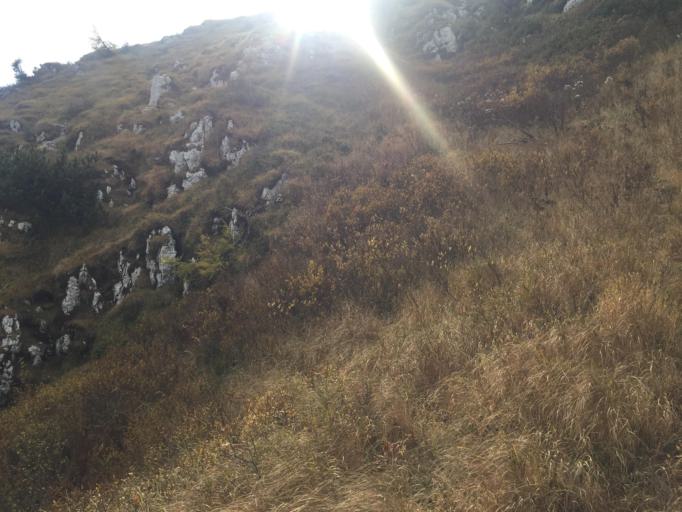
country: IT
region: Friuli Venezia Giulia
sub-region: Provincia di Udine
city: Preone
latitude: 46.3427
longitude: 12.8479
